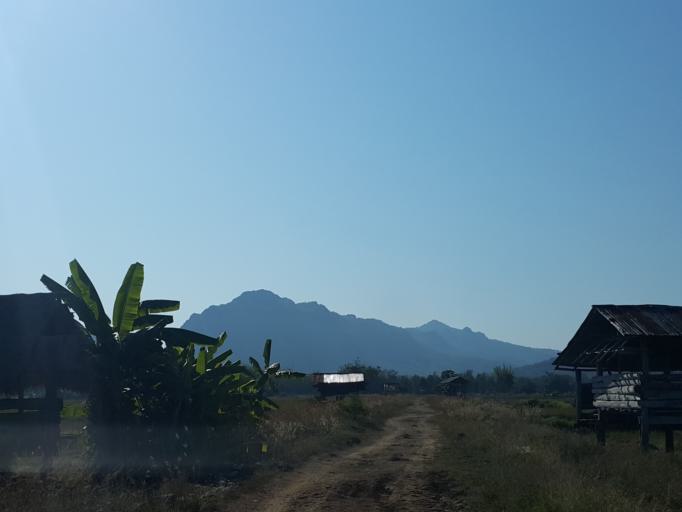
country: TH
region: Sukhothai
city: Thung Saliam
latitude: 17.3176
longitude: 99.4344
